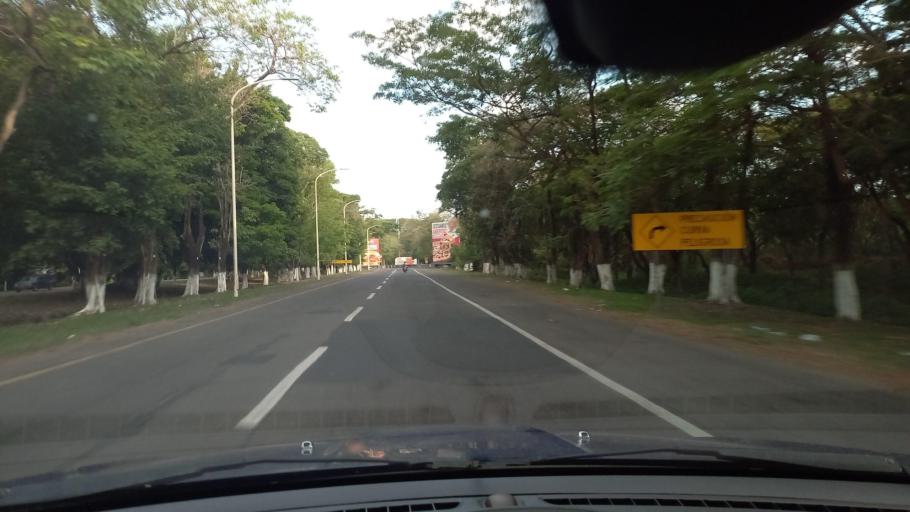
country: SV
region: La Paz
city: El Rosario
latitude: 13.4530
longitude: -89.0603
